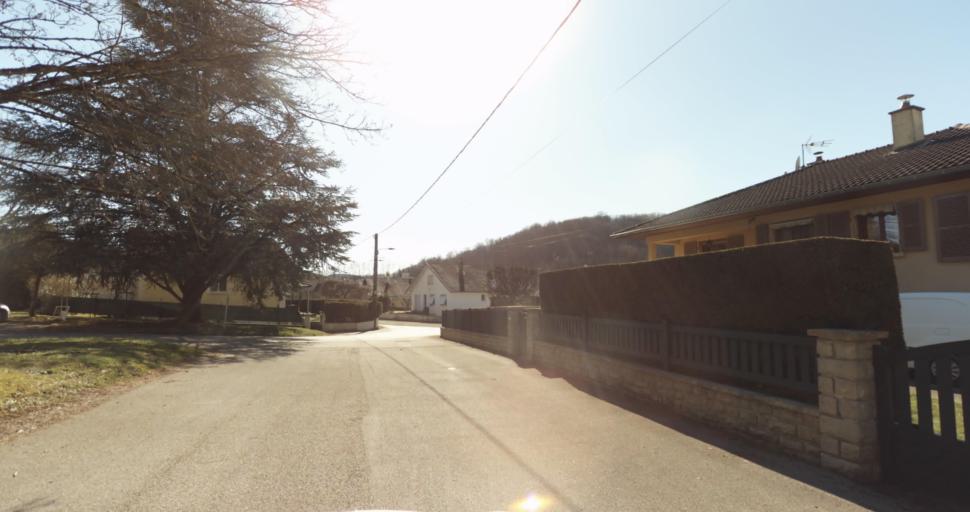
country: FR
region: Franche-Comte
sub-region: Departement du Jura
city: Montmorot
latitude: 46.6757
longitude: 5.5262
